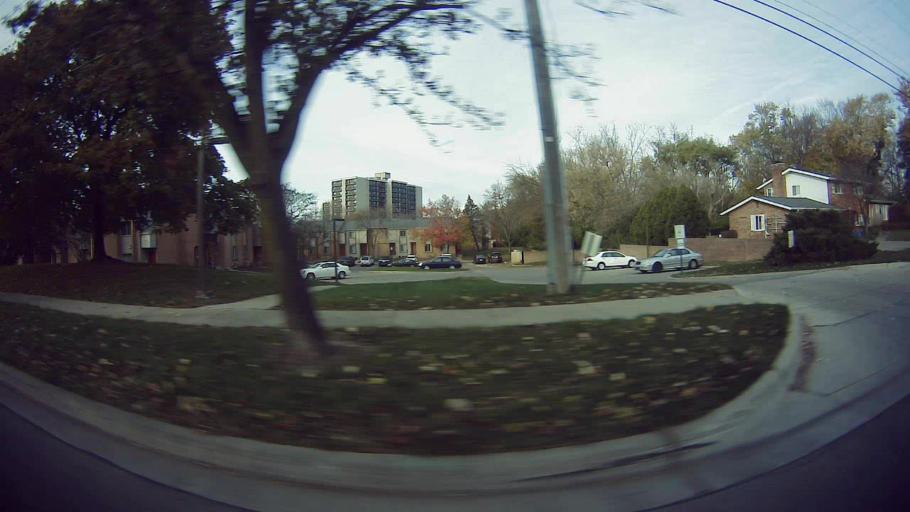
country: US
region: Michigan
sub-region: Oakland County
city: Bingham Farms
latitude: 42.4804
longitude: -83.2795
